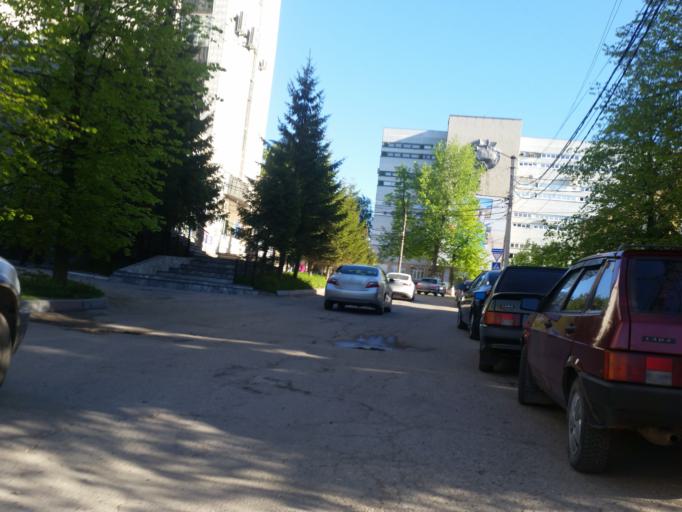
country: RU
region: Ulyanovsk
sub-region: Ulyanovskiy Rayon
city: Ulyanovsk
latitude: 54.3115
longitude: 48.3934
